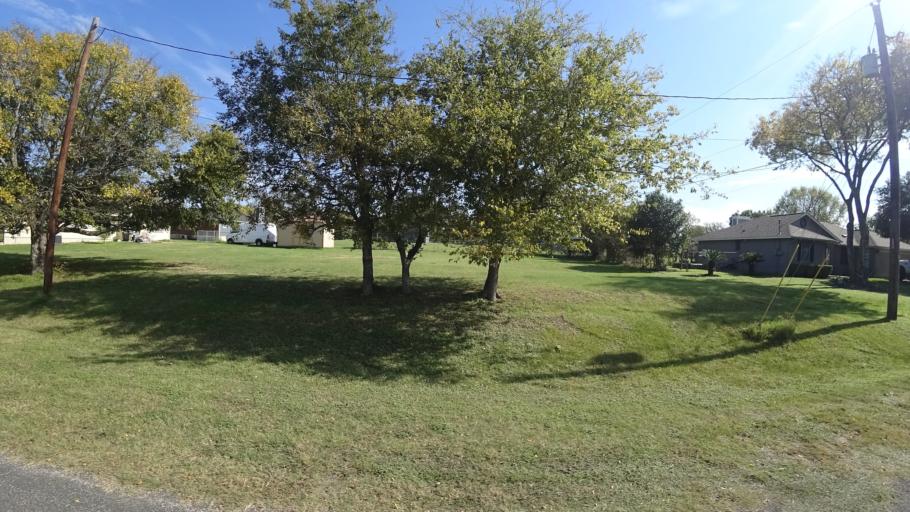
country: US
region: Texas
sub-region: Travis County
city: Pflugerville
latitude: 30.4152
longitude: -97.6312
